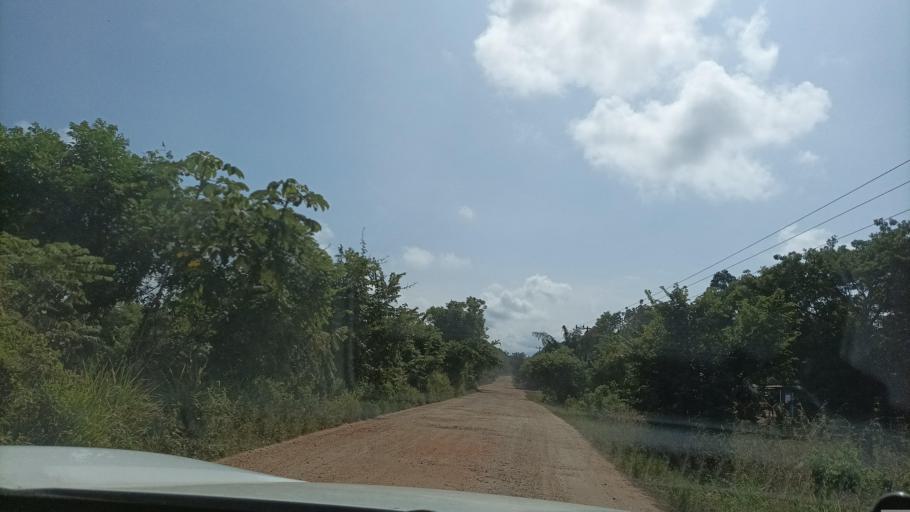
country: MX
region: Veracruz
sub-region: Chinameca
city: Chacalapa
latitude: 18.1251
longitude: -94.6549
